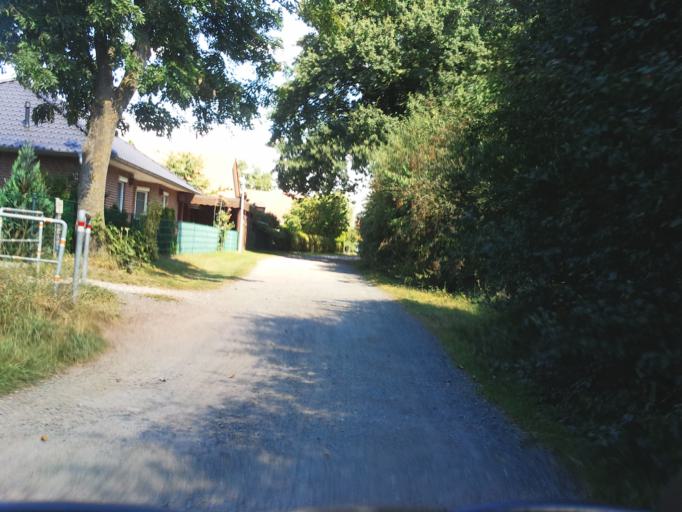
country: DE
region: Lower Saxony
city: Nienburg
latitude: 52.6582
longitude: 9.2388
